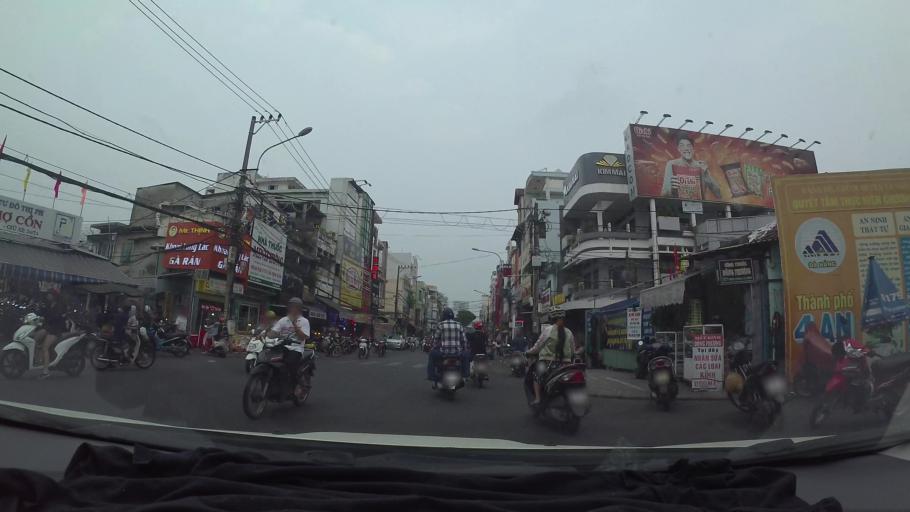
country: VN
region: Da Nang
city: Da Nang
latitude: 16.0674
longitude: 108.2149
